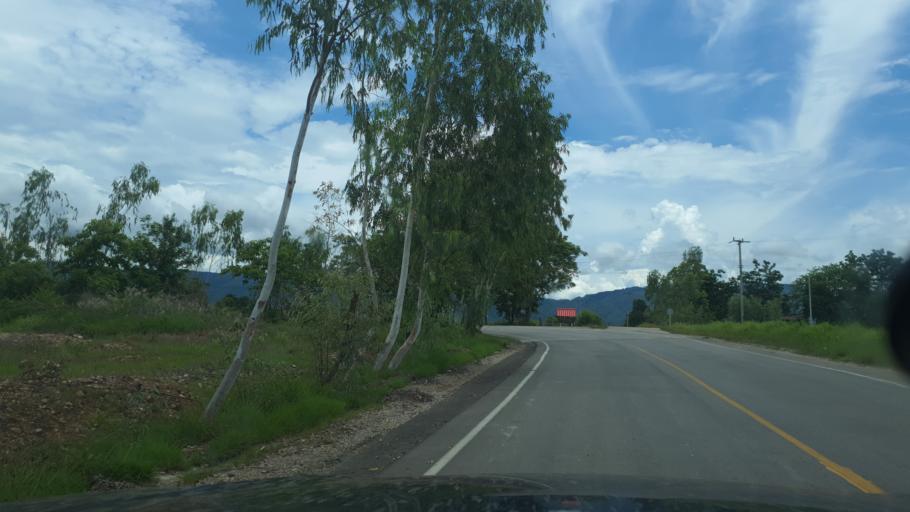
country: TH
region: Lampang
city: Sop Prap
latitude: 17.9141
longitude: 99.3890
